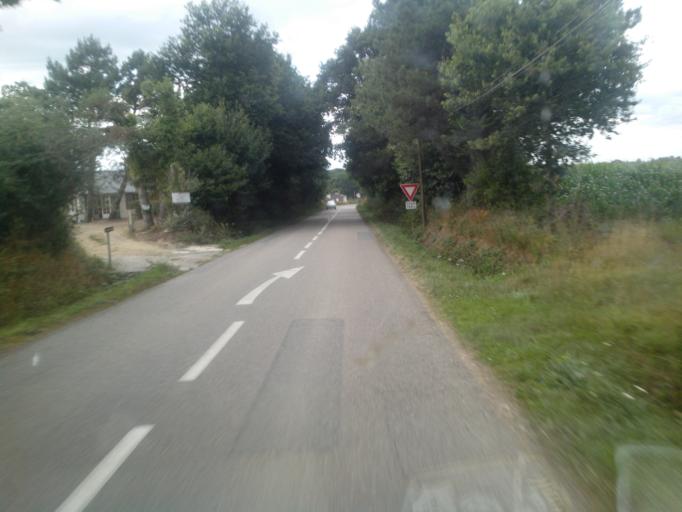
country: FR
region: Brittany
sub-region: Departement d'Ille-et-Vilaine
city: Maxent
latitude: 47.9807
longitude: -2.0249
